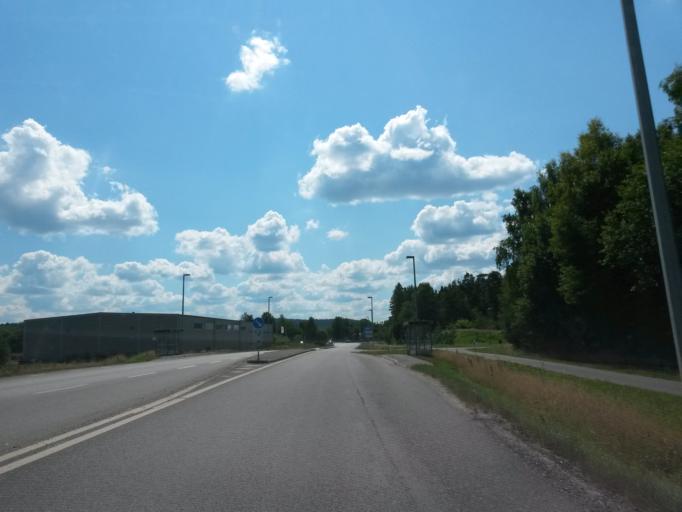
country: SE
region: Vaestra Goetaland
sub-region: Lerums Kommun
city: Stenkullen
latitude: 57.7987
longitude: 12.3077
